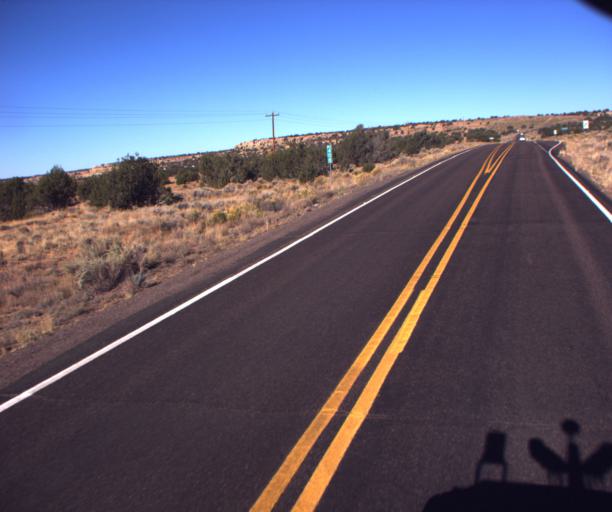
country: US
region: Arizona
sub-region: Navajo County
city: First Mesa
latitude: 35.7612
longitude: -110.1470
